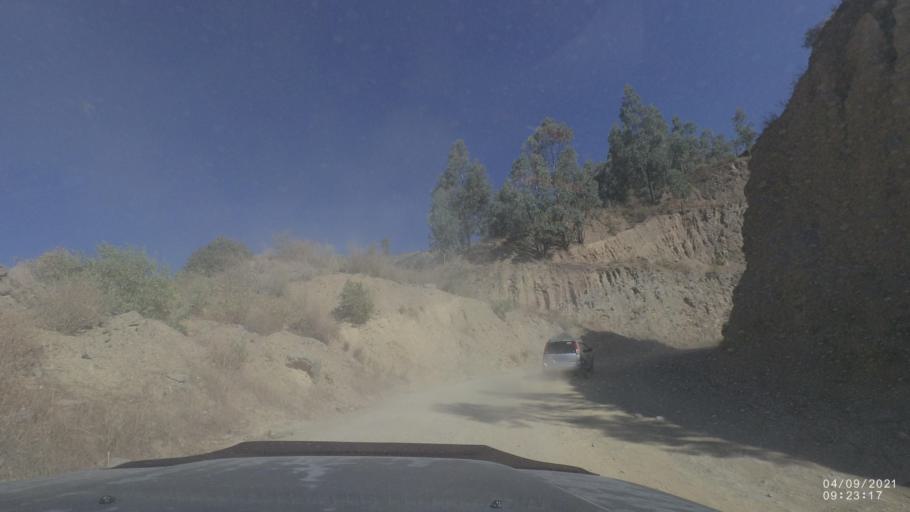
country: BO
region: Cochabamba
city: Sipe Sipe
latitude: -17.3640
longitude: -66.3672
